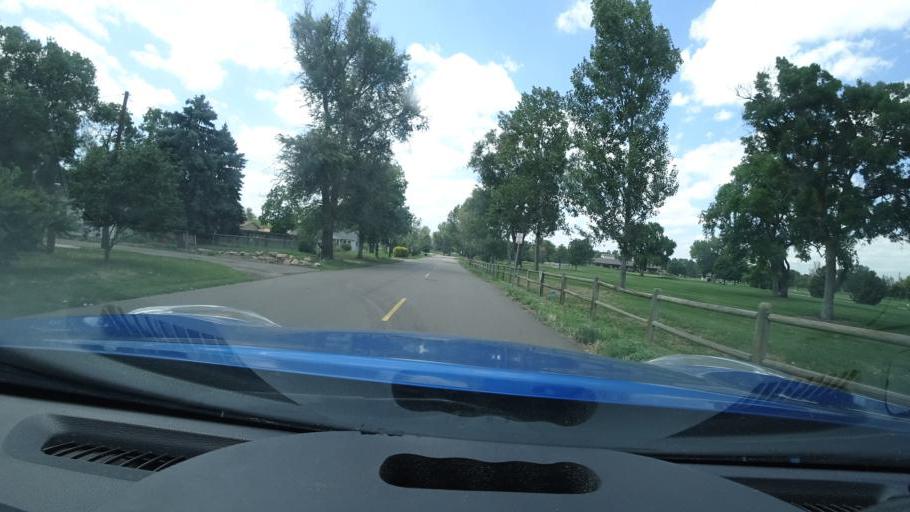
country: US
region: Colorado
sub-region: Arapahoe County
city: Englewood
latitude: 39.6822
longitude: -104.9952
